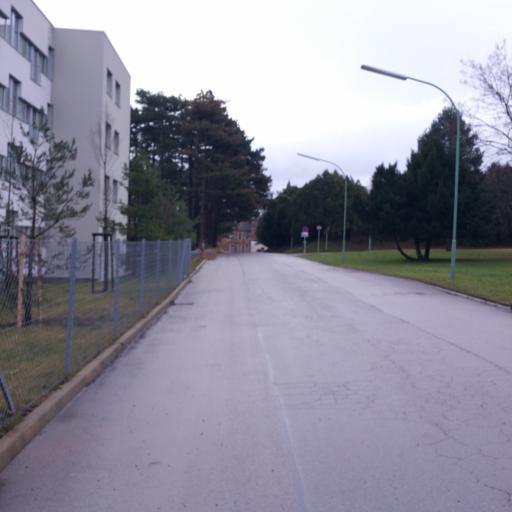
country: AT
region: Vienna
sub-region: Wien Stadt
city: Vienna
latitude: 48.2113
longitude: 16.2839
